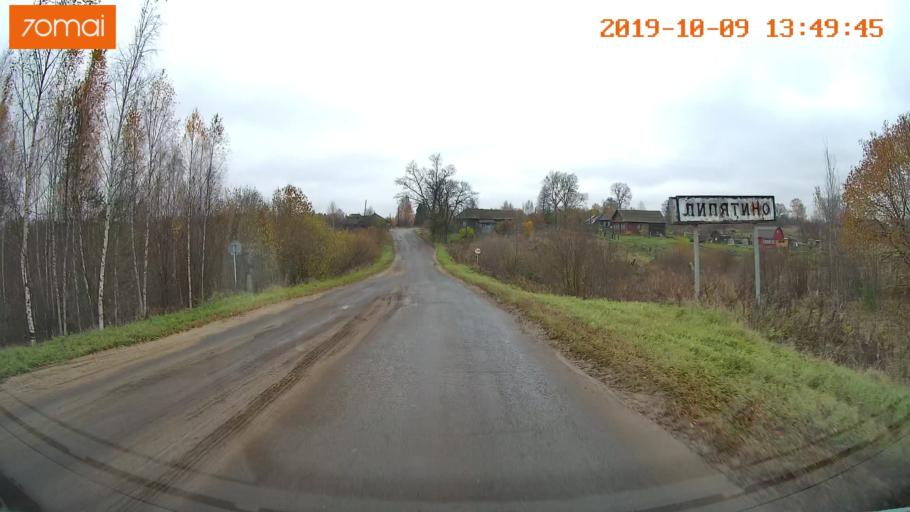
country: RU
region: Kostroma
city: Buy
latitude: 58.4013
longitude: 41.2385
